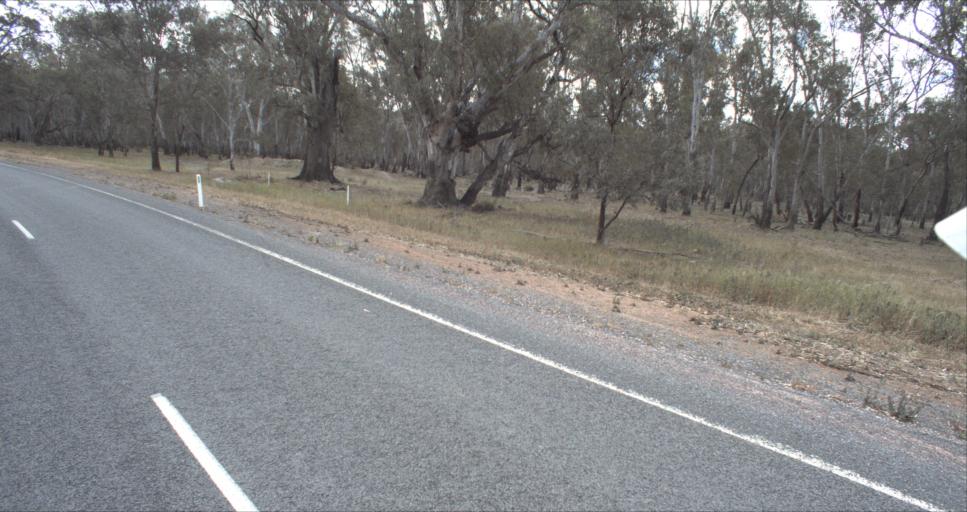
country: AU
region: New South Wales
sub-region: Leeton
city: Leeton
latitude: -34.6408
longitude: 146.3607
